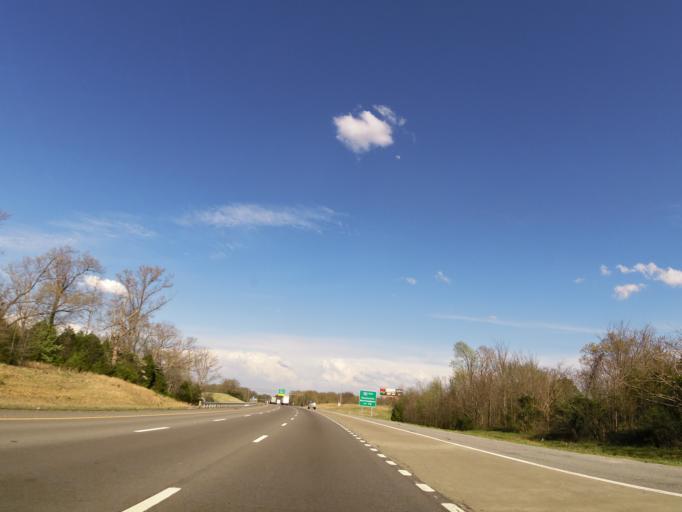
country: US
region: Tennessee
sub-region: Dickson County
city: Burns
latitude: 36.0235
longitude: -87.2897
